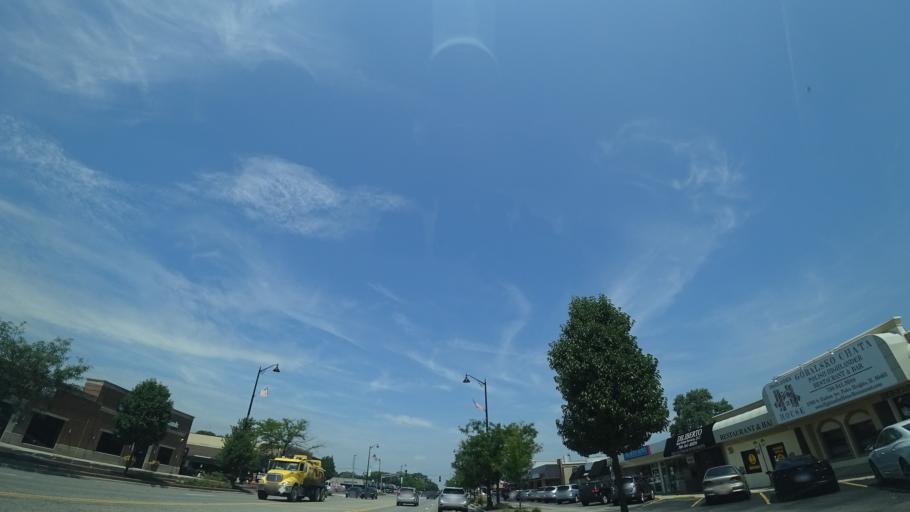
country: US
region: Illinois
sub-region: Cook County
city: Palos Heights
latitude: 41.6666
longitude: -87.7964
